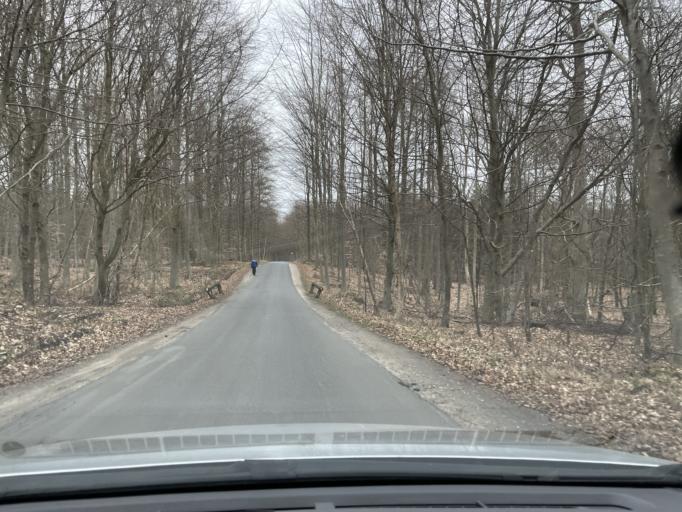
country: DK
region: South Denmark
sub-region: Nyborg Kommune
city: Nyborg
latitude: 55.3391
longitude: 10.8012
